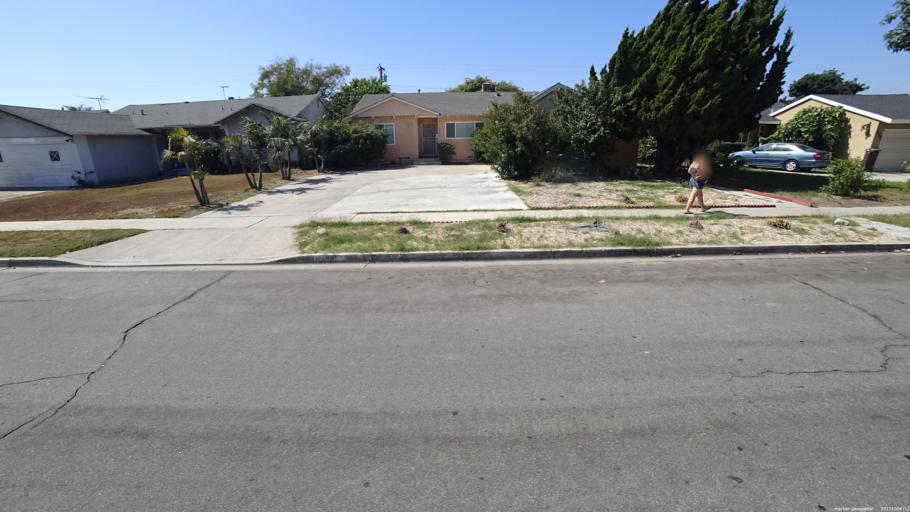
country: US
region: California
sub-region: Orange County
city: Garden Grove
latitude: 33.7872
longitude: -117.9455
